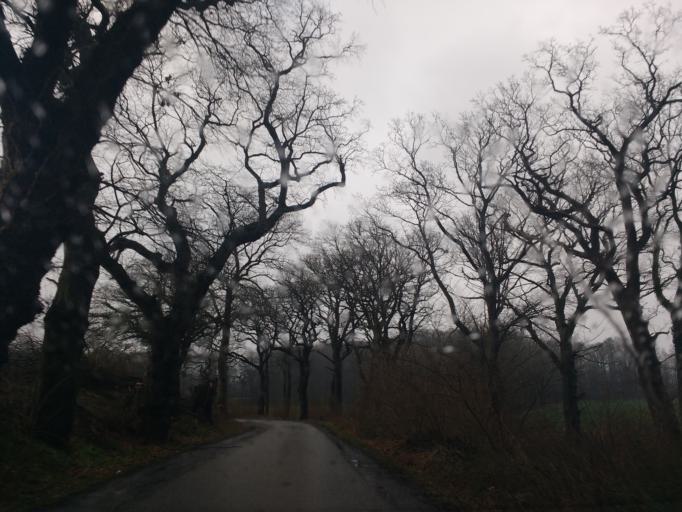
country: DE
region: Schleswig-Holstein
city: Wangels
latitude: 54.3023
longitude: 10.7538
